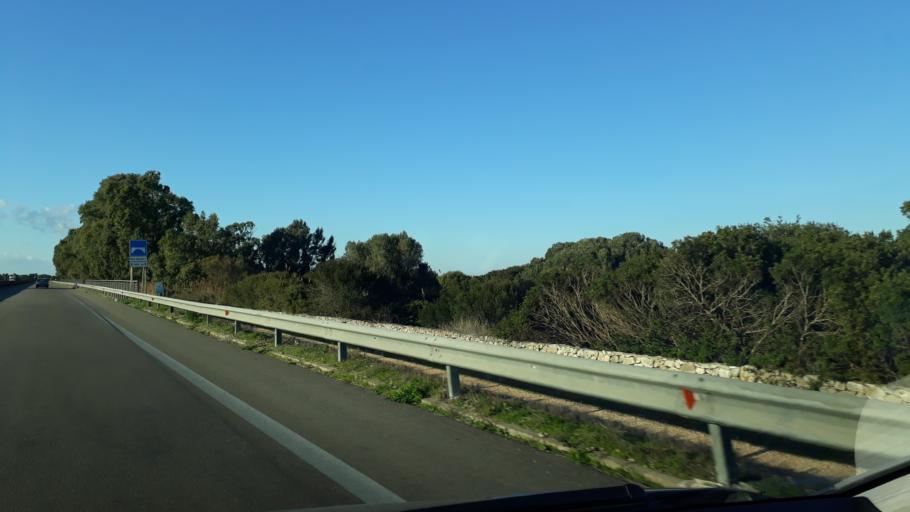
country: IT
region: Apulia
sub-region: Provincia di Brindisi
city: San Vito dei Normanni
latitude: 40.7053
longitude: 17.7972
